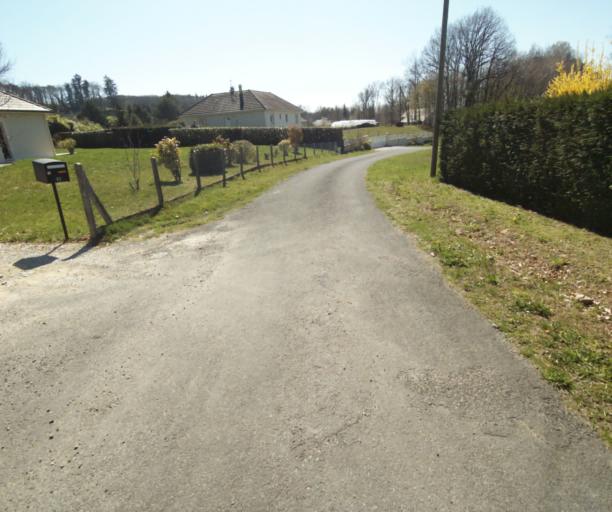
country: FR
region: Limousin
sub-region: Departement de la Correze
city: Saint-Mexant
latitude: 45.2850
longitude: 1.6415
